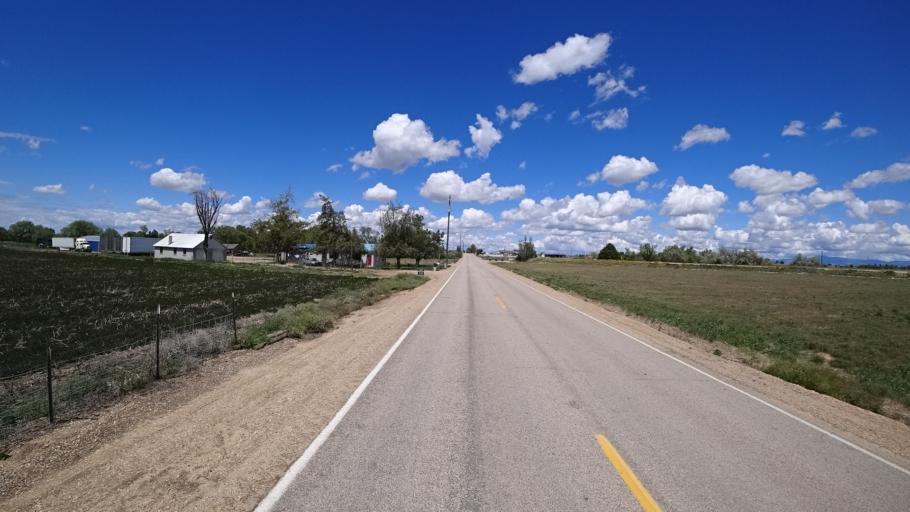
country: US
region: Idaho
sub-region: Ada County
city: Kuna
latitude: 43.5548
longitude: -116.4537
